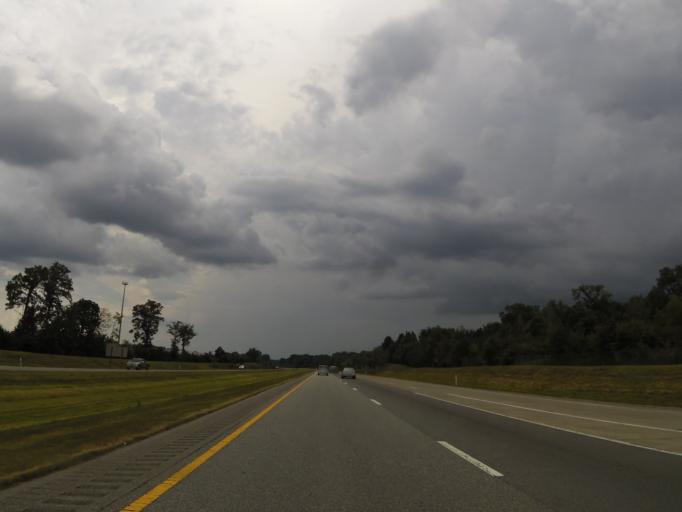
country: US
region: Tennessee
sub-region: Wilson County
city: Rural Hill
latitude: 36.0646
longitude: -86.4312
